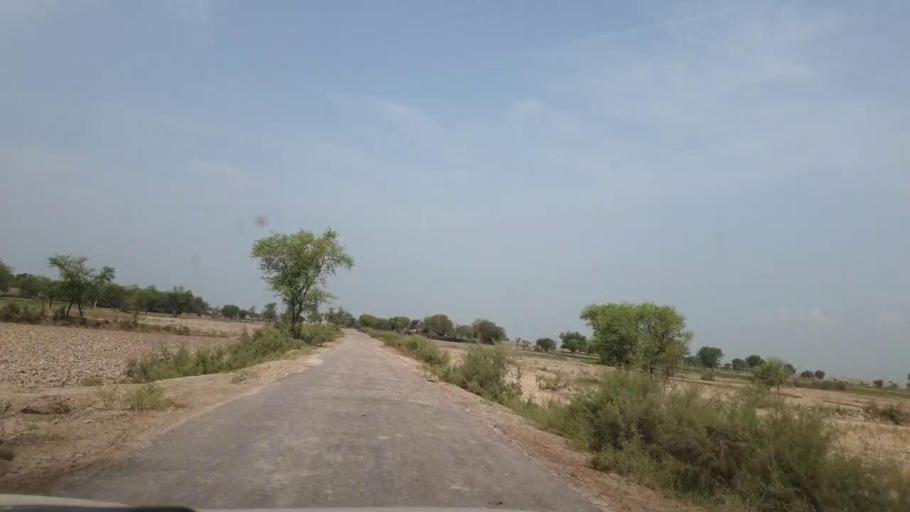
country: PK
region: Sindh
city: Dokri
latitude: 27.4022
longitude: 68.2495
